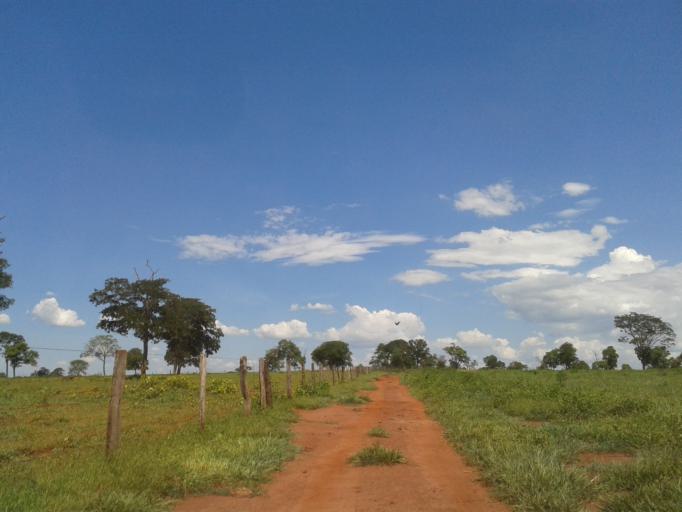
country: BR
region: Minas Gerais
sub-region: Santa Vitoria
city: Santa Vitoria
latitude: -19.1045
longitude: -50.5212
